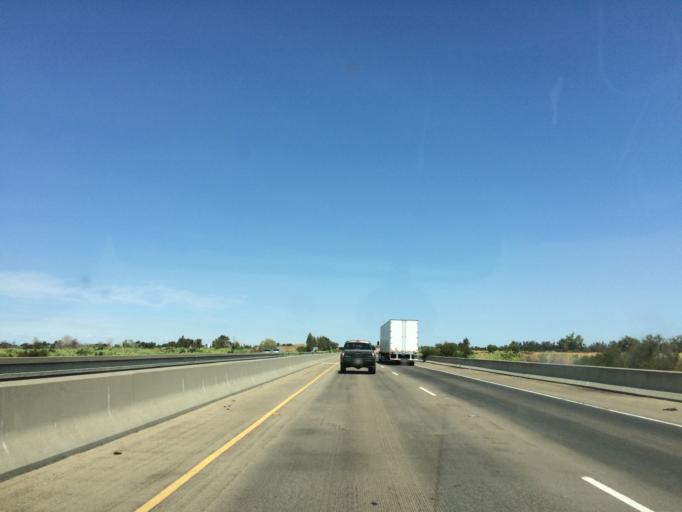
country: US
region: California
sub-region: Glenn County
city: Orland
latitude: 39.7702
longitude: -122.2049
